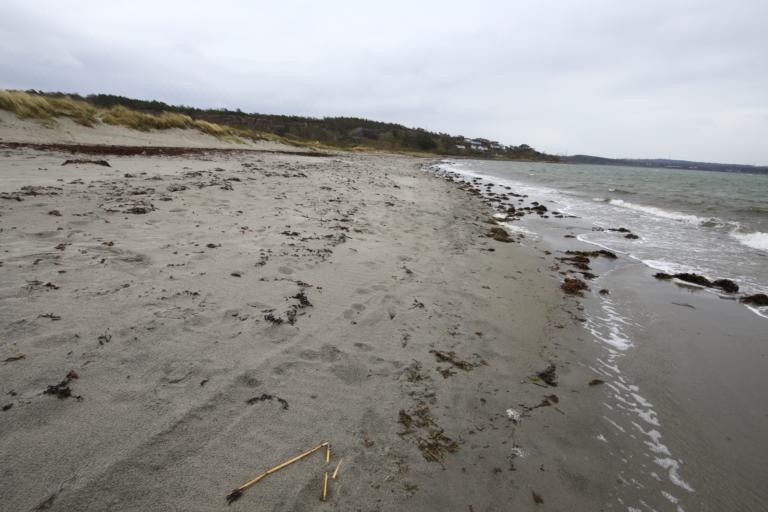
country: SE
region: Halland
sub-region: Kungsbacka Kommun
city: Frillesas
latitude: 57.2967
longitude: 12.1645
